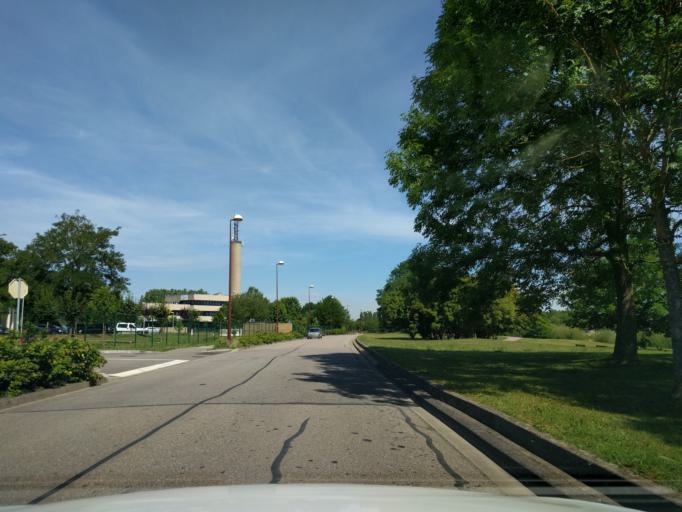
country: FR
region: Lorraine
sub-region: Departement de la Moselle
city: Peltre
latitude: 49.1017
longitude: 6.2164
